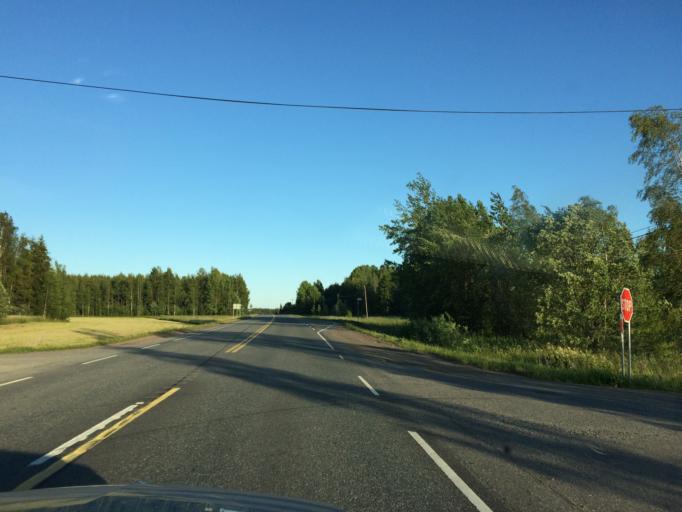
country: FI
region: Haeme
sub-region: Haemeenlinna
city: Tervakoski
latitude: 60.8088
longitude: 24.6498
